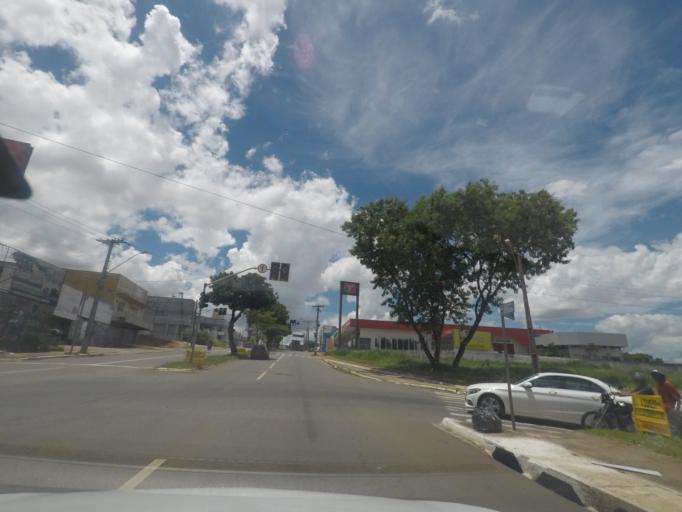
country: BR
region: Goias
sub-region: Goiania
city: Goiania
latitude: -16.6743
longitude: -49.2967
